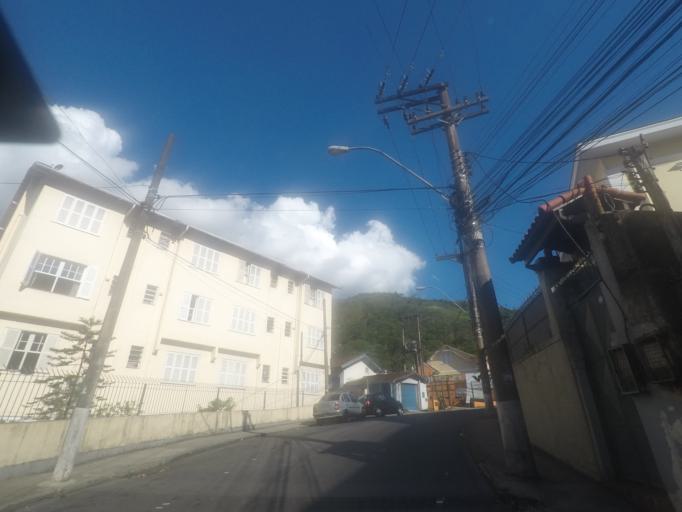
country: BR
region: Rio de Janeiro
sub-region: Petropolis
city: Petropolis
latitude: -22.5085
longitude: -43.1678
